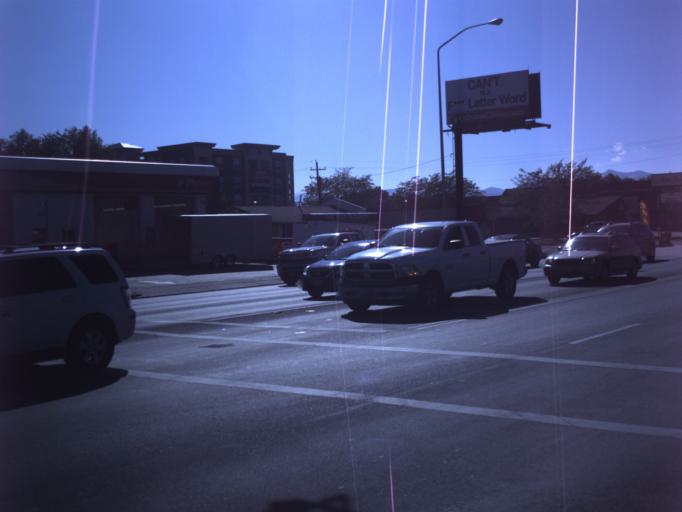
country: US
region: Utah
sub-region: Salt Lake County
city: Centerfield
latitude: 40.6999
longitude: -111.8912
